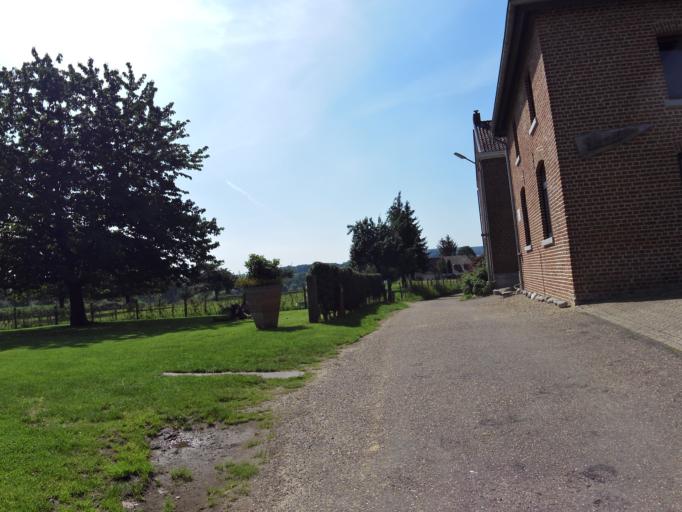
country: BE
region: Wallonia
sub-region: Province de Liege
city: Plombieres
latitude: 50.7741
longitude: 5.9173
